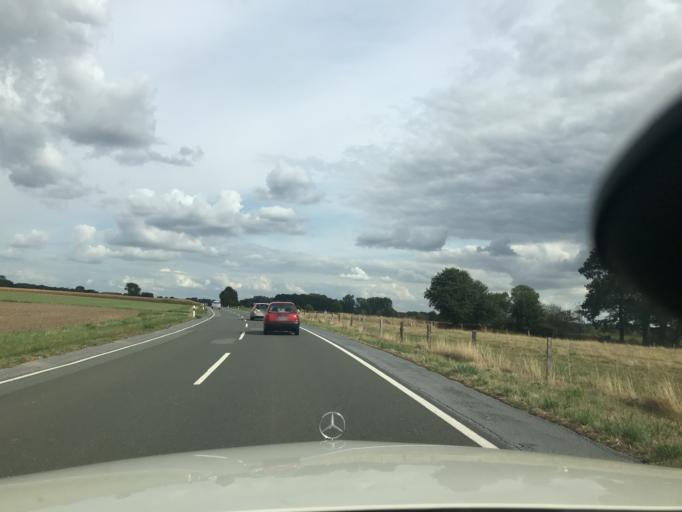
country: DE
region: North Rhine-Westphalia
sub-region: Regierungsbezirk Arnsberg
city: Bad Sassendorf
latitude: 51.6631
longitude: 8.1985
